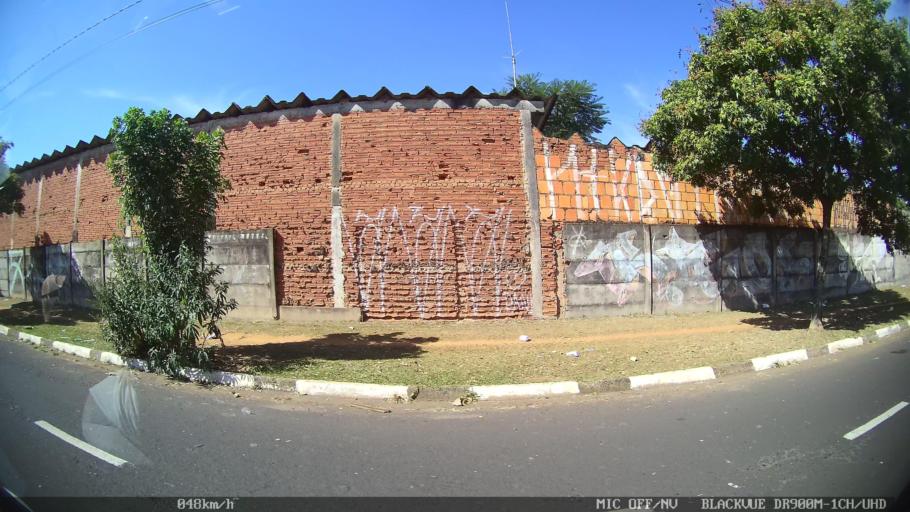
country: BR
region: Sao Paulo
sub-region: Franca
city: Franca
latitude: -20.5058
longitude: -47.3989
